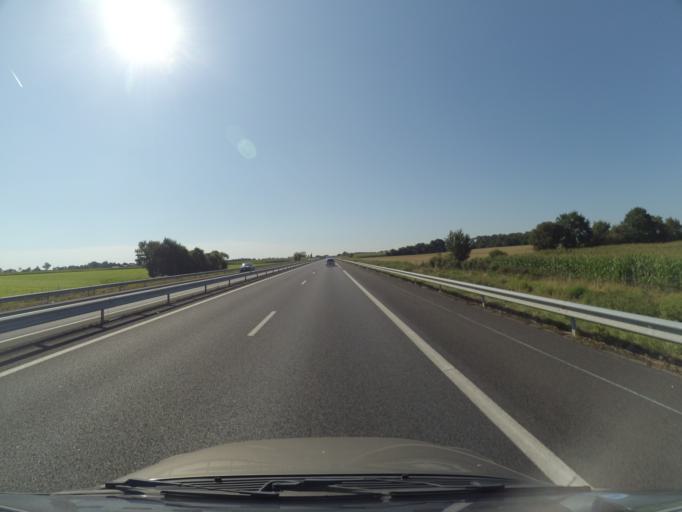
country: FR
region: Pays de la Loire
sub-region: Departement de la Vendee
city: Bouffere
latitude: 46.9278
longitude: -1.3360
